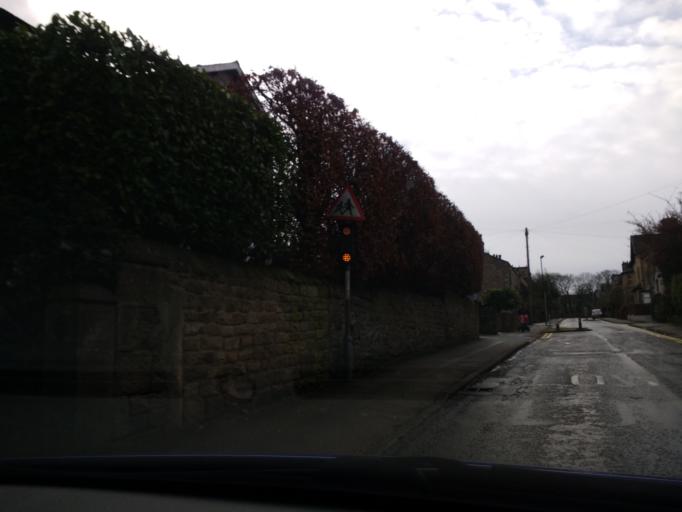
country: GB
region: England
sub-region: Lancashire
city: Lancaster
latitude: 54.0502
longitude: -2.7861
